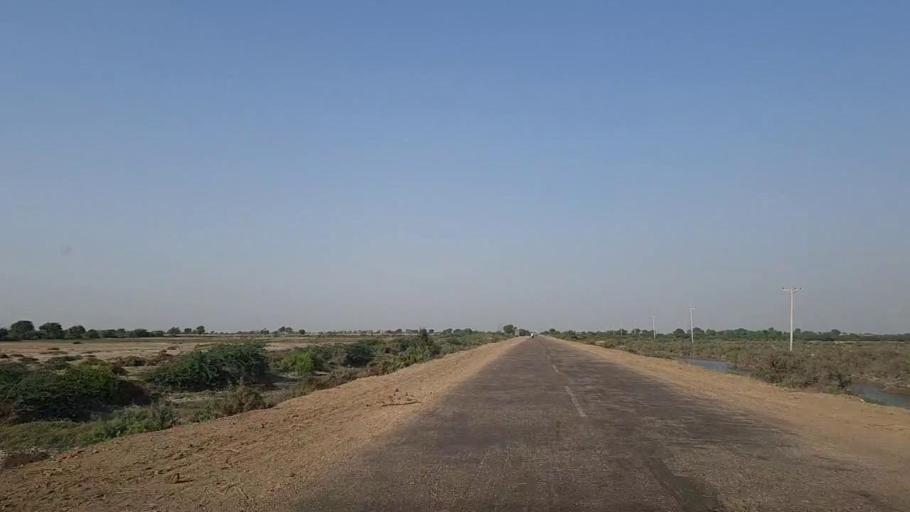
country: PK
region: Sindh
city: Mirpur Batoro
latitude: 24.6178
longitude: 68.4055
